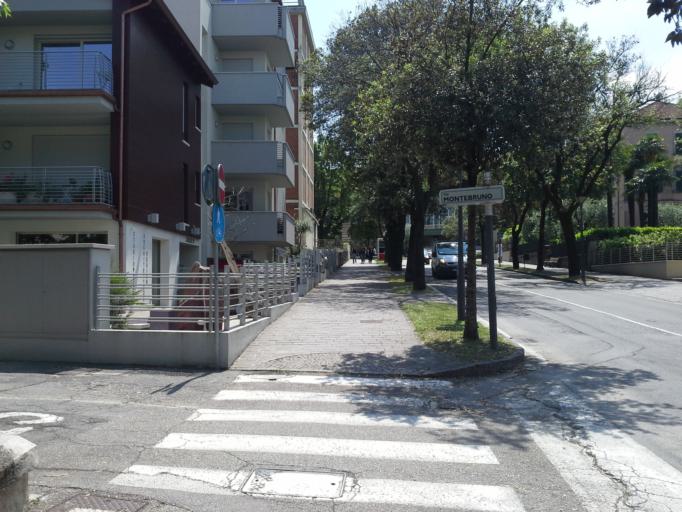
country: IT
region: Lombardy
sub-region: Provincia di Brescia
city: Desenzano del Garda
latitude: 45.4638
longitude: 10.5367
